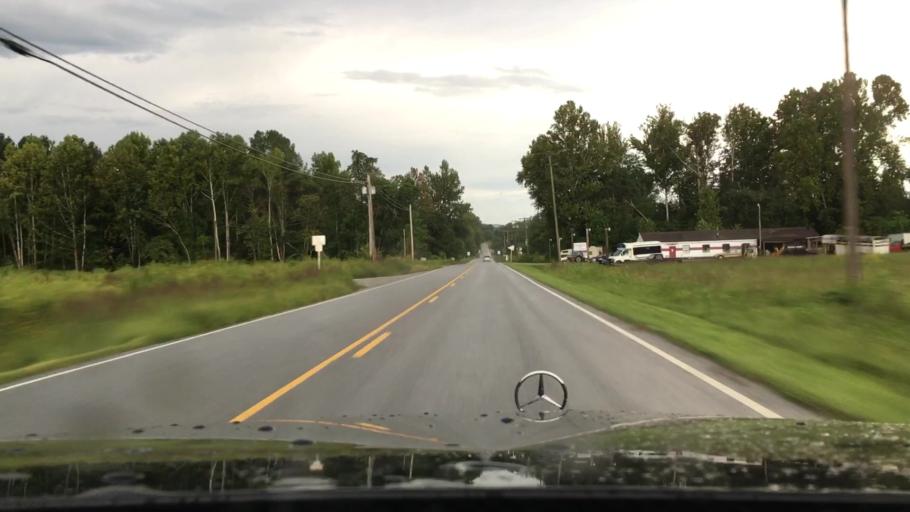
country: US
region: Virginia
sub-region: Amherst County
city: Amherst
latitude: 37.7075
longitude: -79.0237
